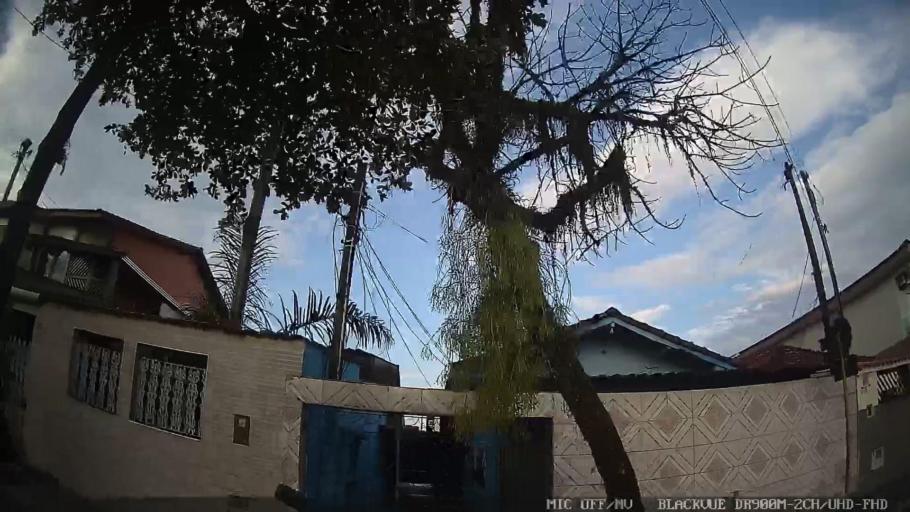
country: BR
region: Sao Paulo
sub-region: Cubatao
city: Cubatao
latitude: -23.8979
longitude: -46.4240
